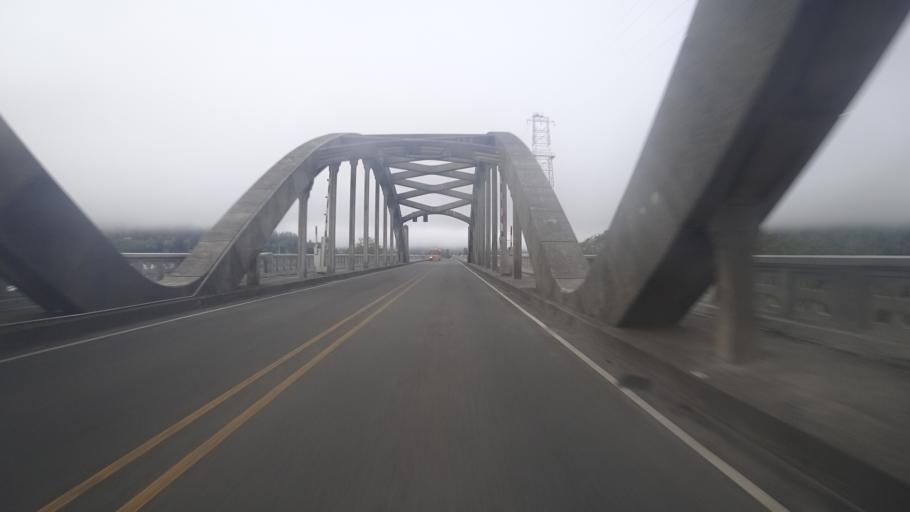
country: US
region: Oregon
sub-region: Douglas County
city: Reedsport
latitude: 43.7088
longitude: -124.1015
